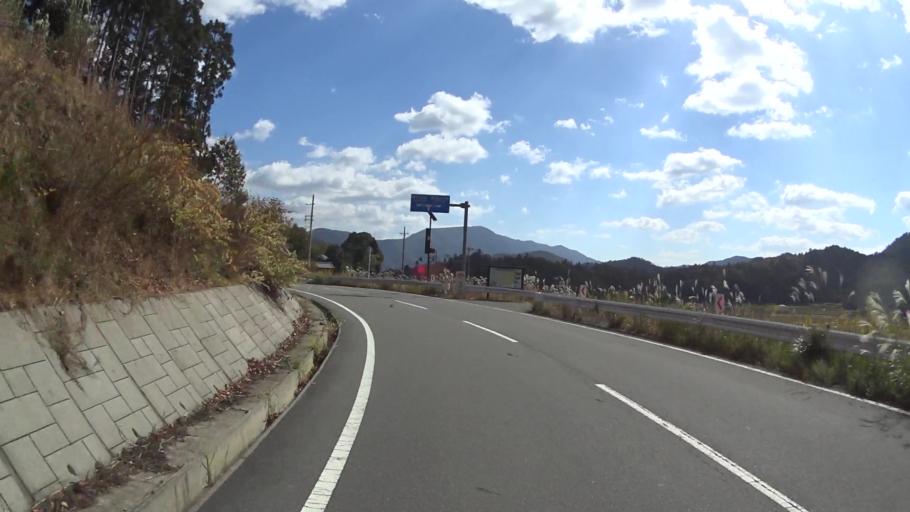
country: JP
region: Kyoto
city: Kameoka
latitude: 35.1122
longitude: 135.5726
